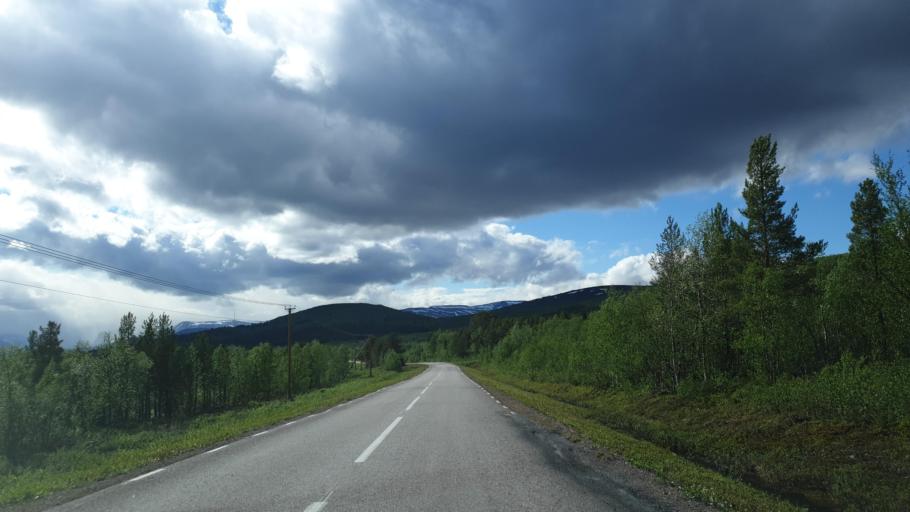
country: SE
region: Norrbotten
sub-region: Kiruna Kommun
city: Kiruna
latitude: 67.8673
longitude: 19.3847
